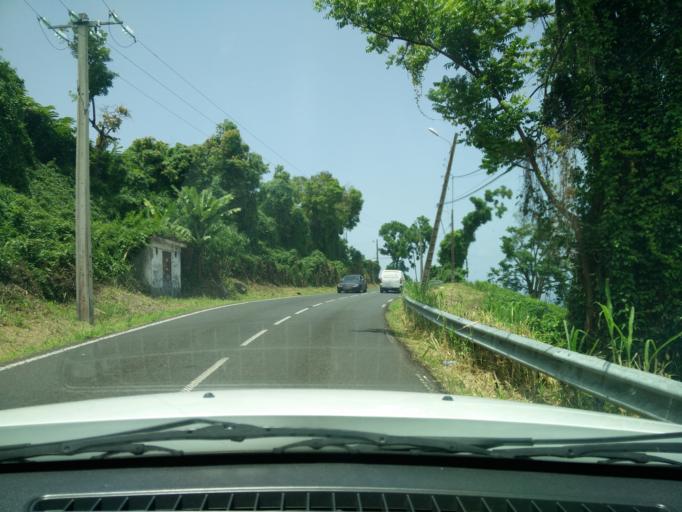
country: GP
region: Guadeloupe
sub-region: Guadeloupe
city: Trois-Rivieres
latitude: 15.9761
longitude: -61.6320
